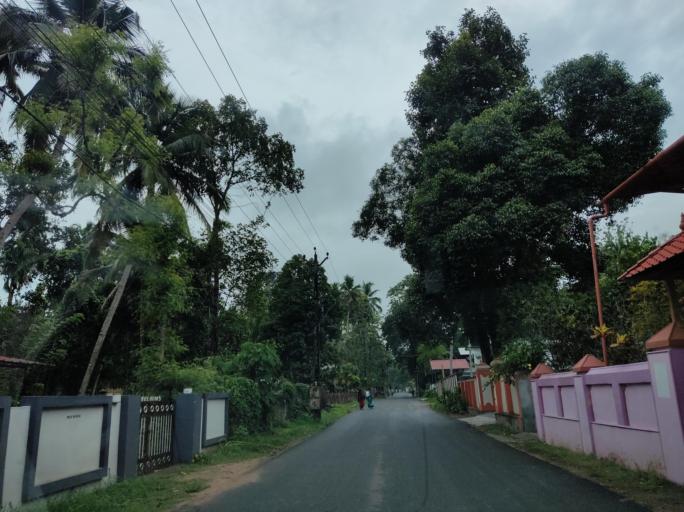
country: IN
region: Kerala
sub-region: Alappuzha
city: Mavelikara
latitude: 9.2499
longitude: 76.5294
